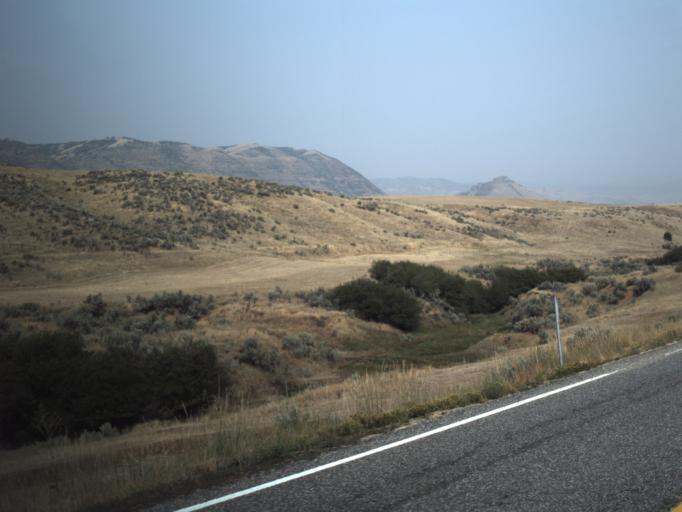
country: US
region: Utah
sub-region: Summit County
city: Coalville
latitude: 41.0055
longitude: -111.5192
